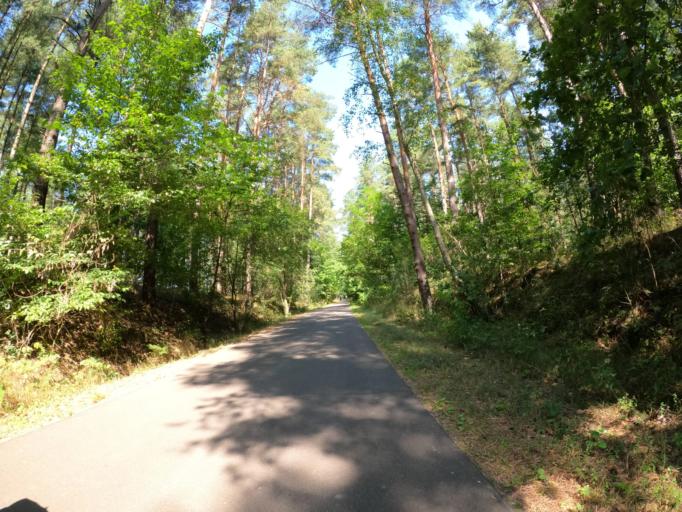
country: DE
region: Brandenburg
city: Templin
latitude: 53.1664
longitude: 13.5207
